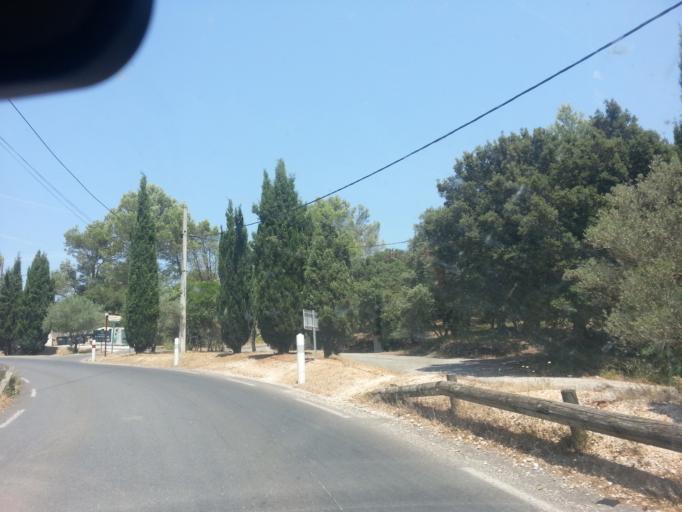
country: FR
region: Provence-Alpes-Cote d'Azur
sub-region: Departement du Var
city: Pignans
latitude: 43.3062
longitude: 6.2325
